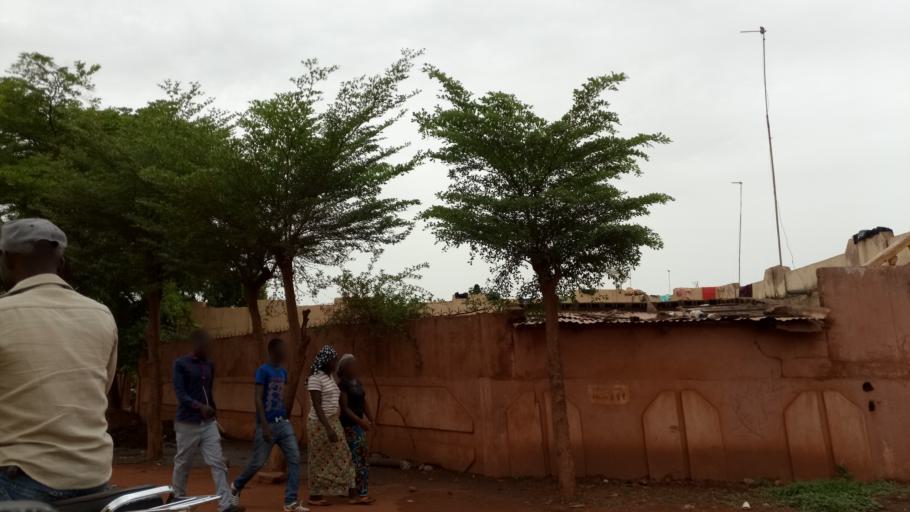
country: ML
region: Bamako
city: Bamako
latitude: 12.5852
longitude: -7.9973
